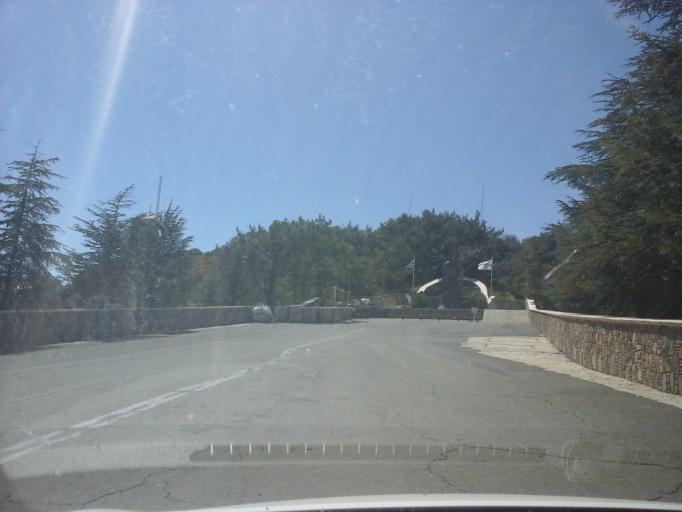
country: CY
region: Lefkosia
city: Kakopetria
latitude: 34.9840
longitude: 32.7332
